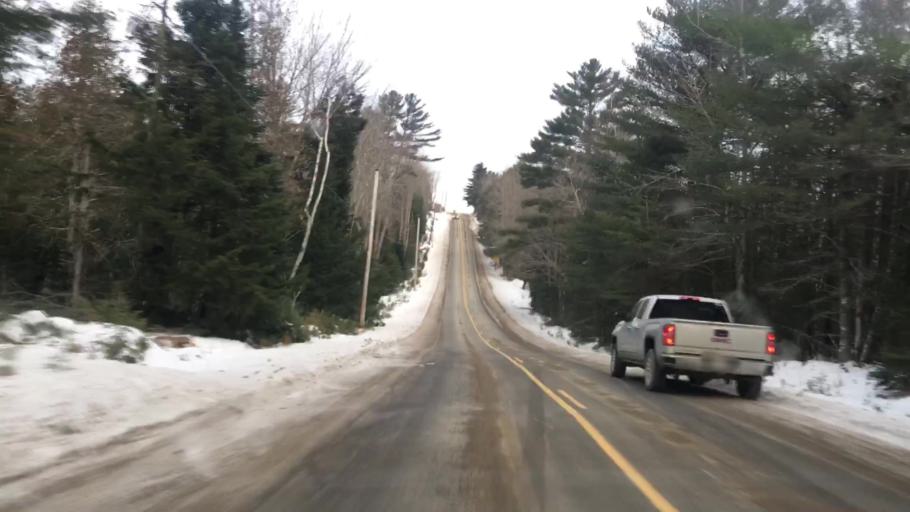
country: US
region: Maine
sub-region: Hancock County
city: Franklin
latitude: 44.8409
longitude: -68.3244
